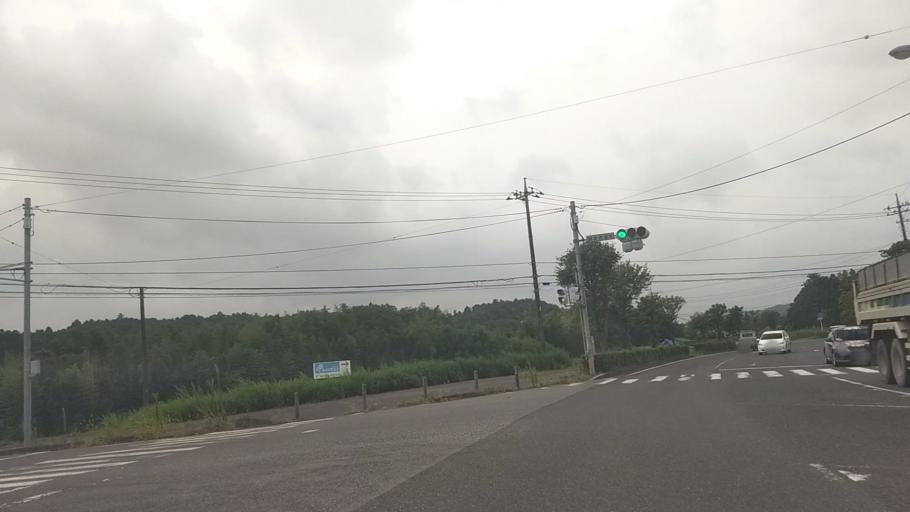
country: JP
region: Chiba
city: Kisarazu
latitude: 35.3745
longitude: 140.0124
